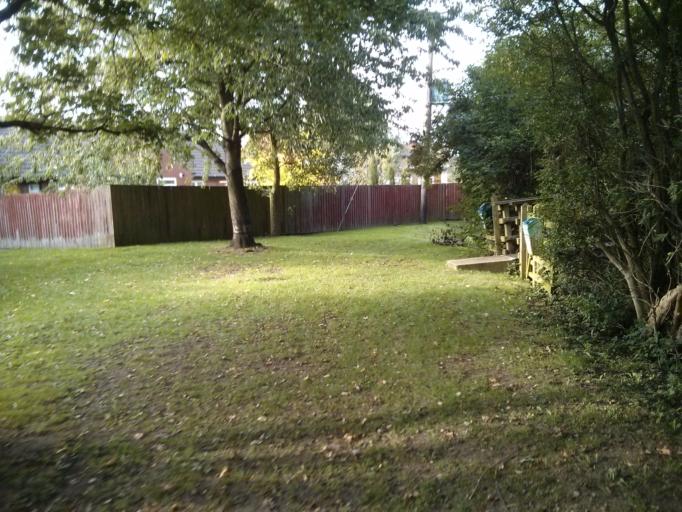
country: GB
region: England
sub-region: Lincolnshire
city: Long Bennington
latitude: 52.9439
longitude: -0.8058
